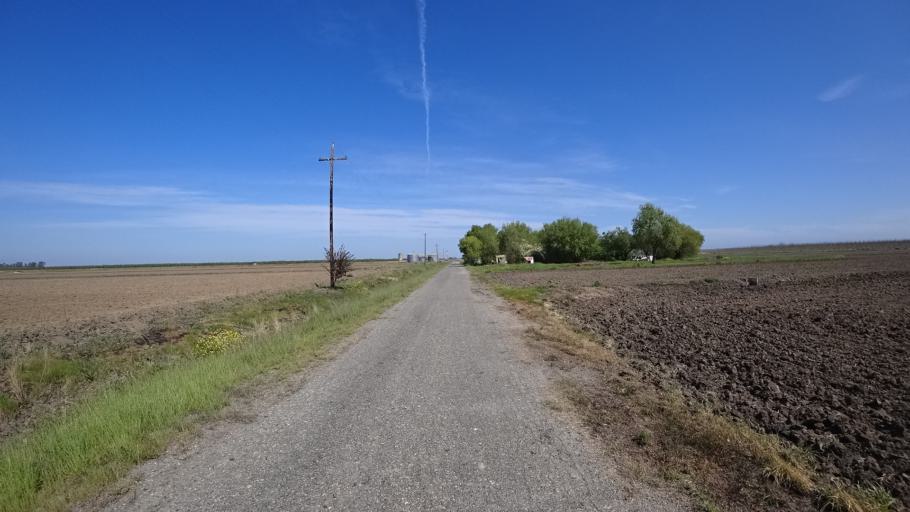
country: US
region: California
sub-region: Glenn County
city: Hamilton City
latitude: 39.6254
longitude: -122.0556
